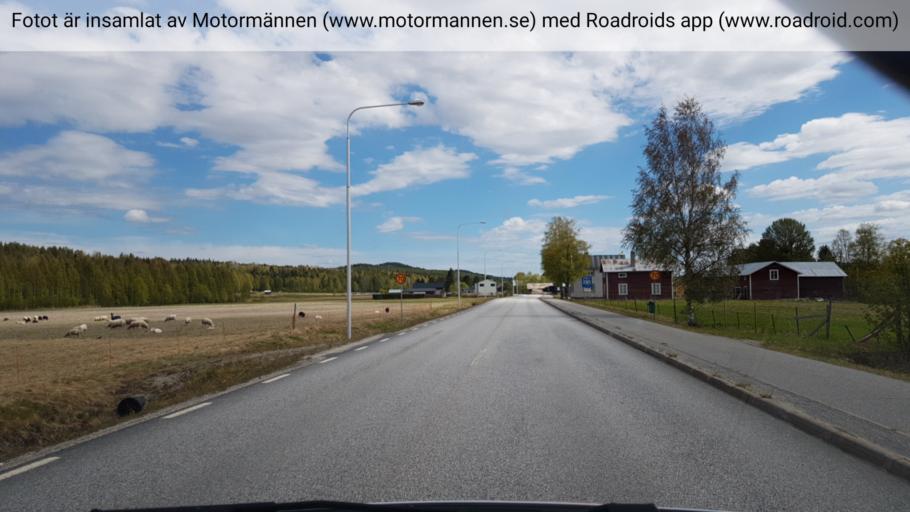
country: SE
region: Vaesterbotten
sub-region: Bjurholms Kommun
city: Bjurholm
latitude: 64.2575
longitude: 19.2913
